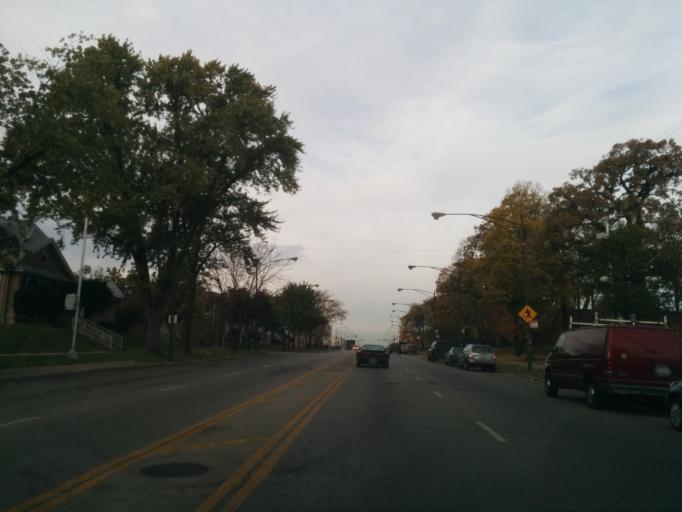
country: US
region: Illinois
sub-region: Cook County
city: Elmwood Park
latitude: 41.9238
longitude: -87.7821
